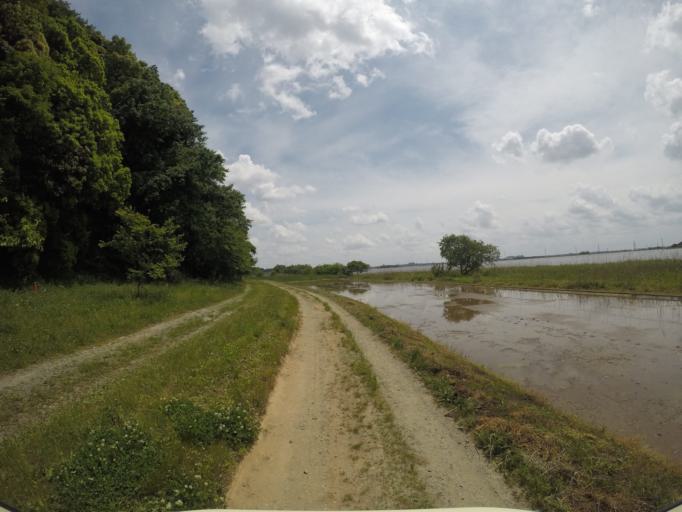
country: JP
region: Ibaraki
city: Ushiku
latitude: 35.9541
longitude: 140.1283
